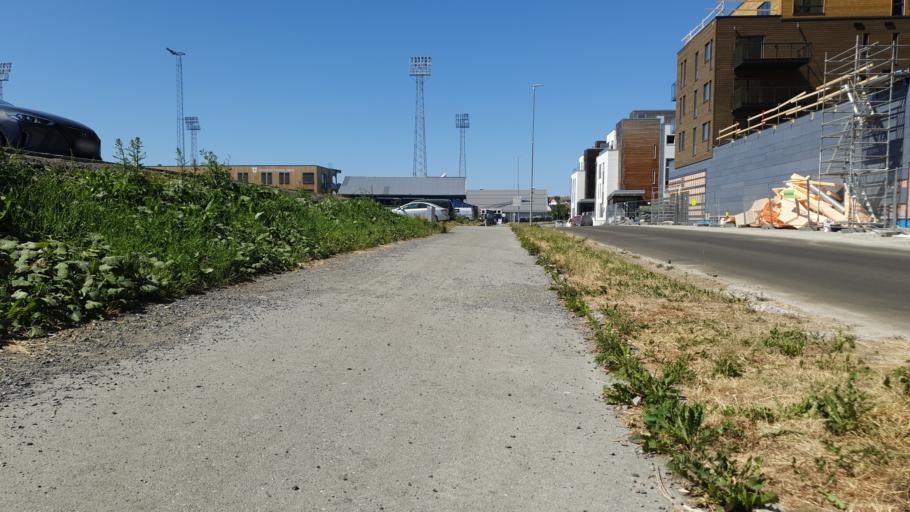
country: NO
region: Sor-Trondelag
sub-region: Trondheim
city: Trondheim
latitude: 63.4285
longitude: 10.5284
